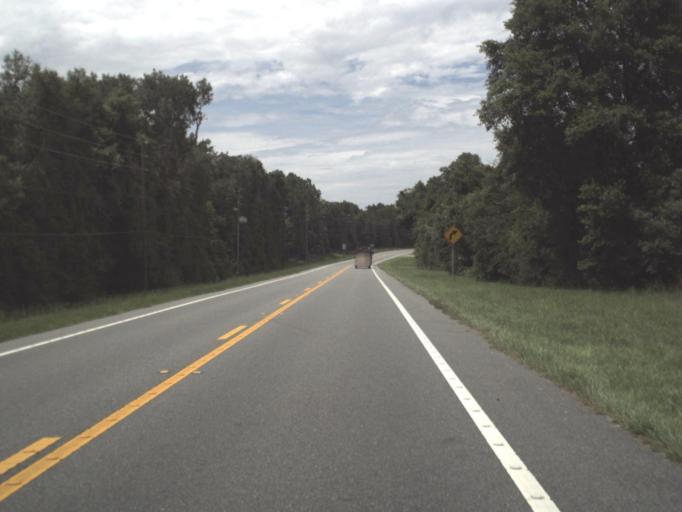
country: US
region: Florida
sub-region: Citrus County
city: Hernando
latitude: 28.9568
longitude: -82.3775
